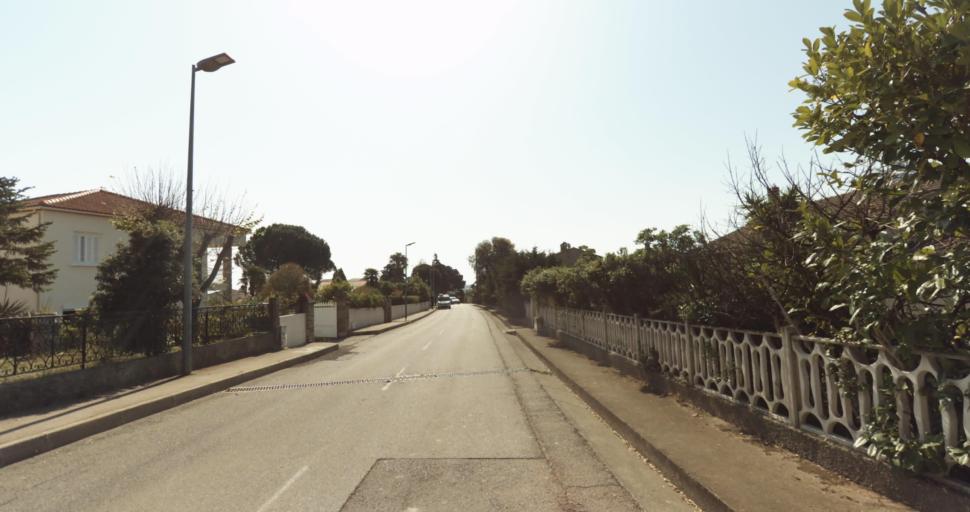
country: FR
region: Corsica
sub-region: Departement de la Haute-Corse
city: Biguglia
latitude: 42.6218
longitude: 9.4293
